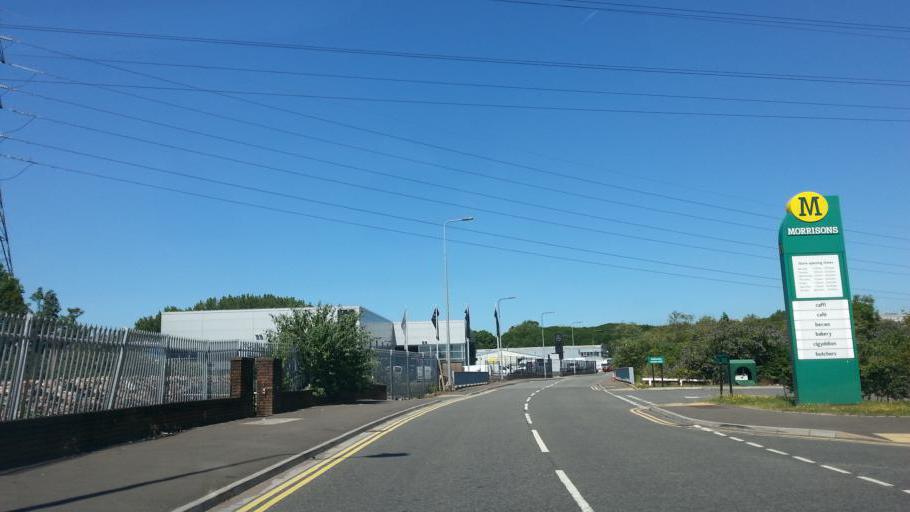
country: GB
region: Wales
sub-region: Cardiff
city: Cardiff
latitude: 51.4995
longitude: -3.1426
